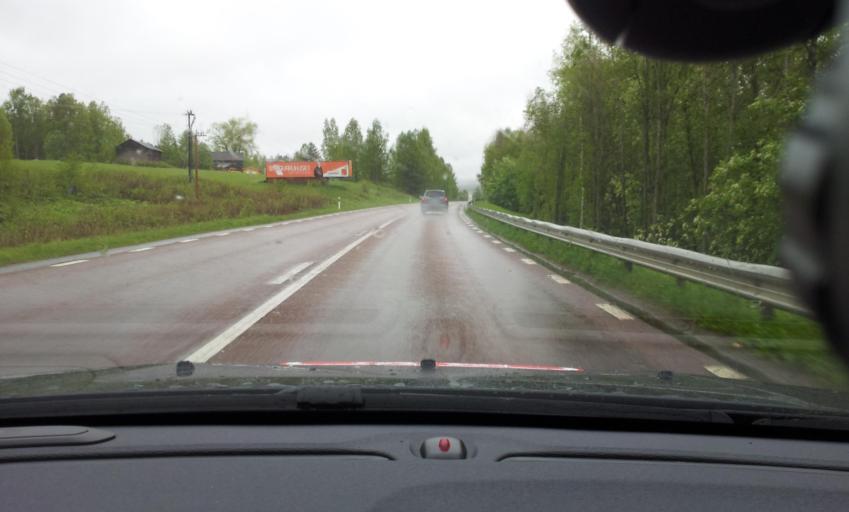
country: SE
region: Jaemtland
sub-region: Bergs Kommun
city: Hoverberg
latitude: 62.7722
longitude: 14.4444
